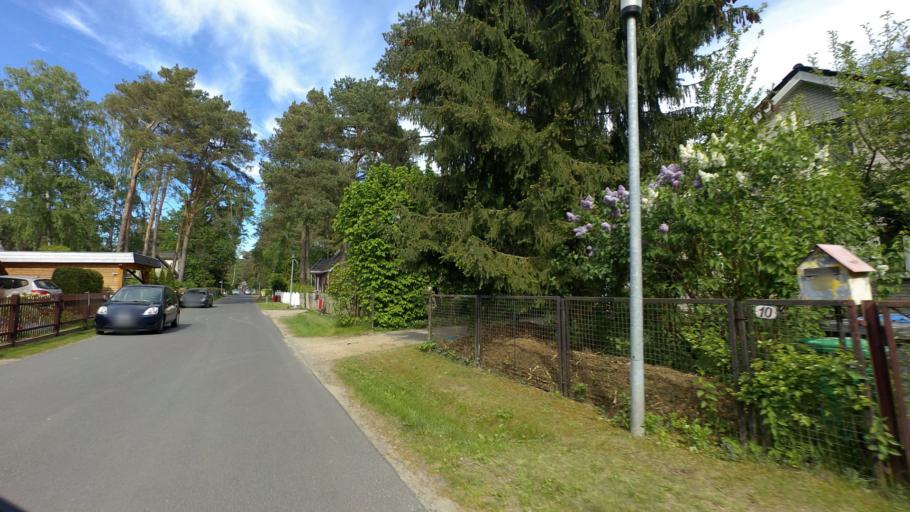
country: DE
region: Berlin
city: Lichtenrade
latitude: 52.3540
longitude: 13.4377
